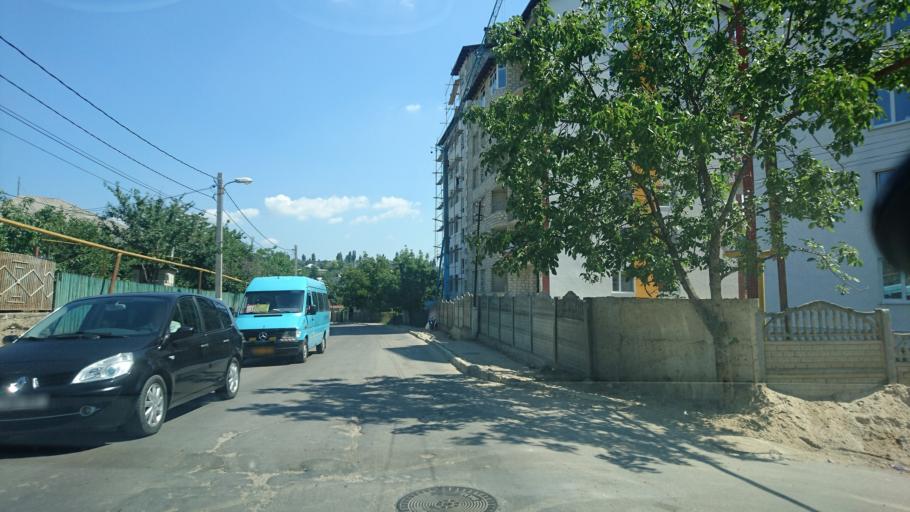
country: MD
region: Chisinau
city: Vatra
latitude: 47.0250
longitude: 28.7700
